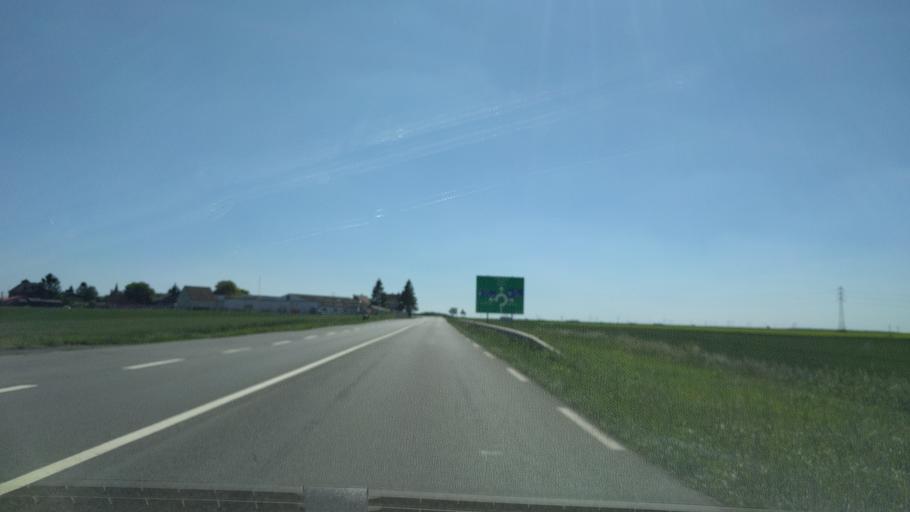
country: FR
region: Picardie
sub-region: Departement de la Somme
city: Peronne
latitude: 49.8805
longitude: 2.8991
